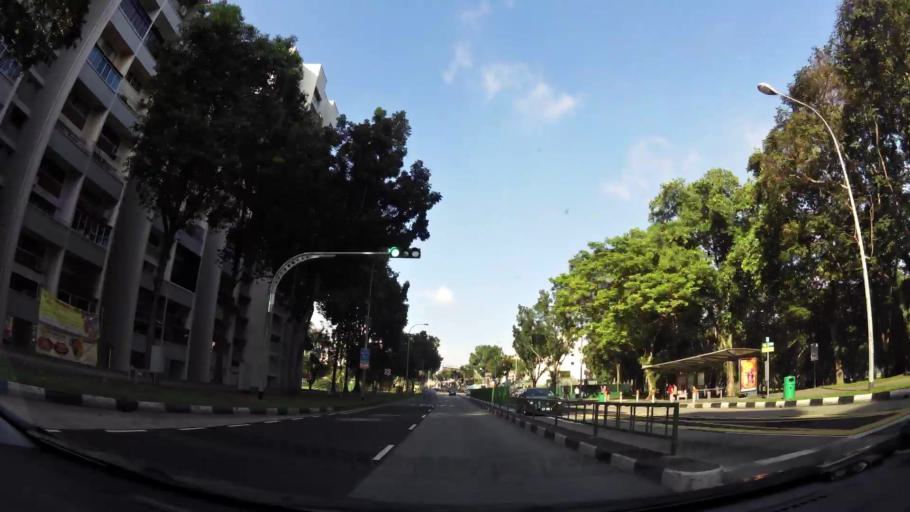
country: SG
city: Singapore
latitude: 1.3382
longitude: 103.9251
